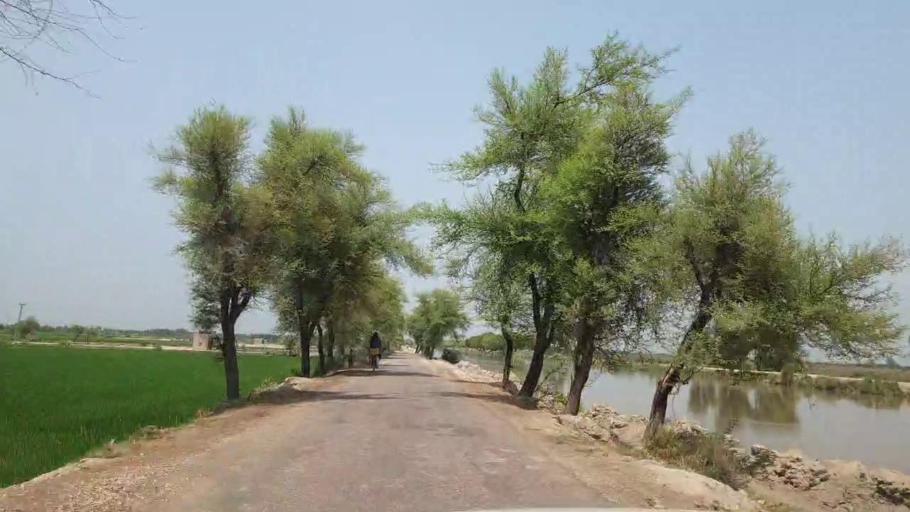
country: PK
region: Sindh
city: Dokri
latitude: 27.3445
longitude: 68.1115
